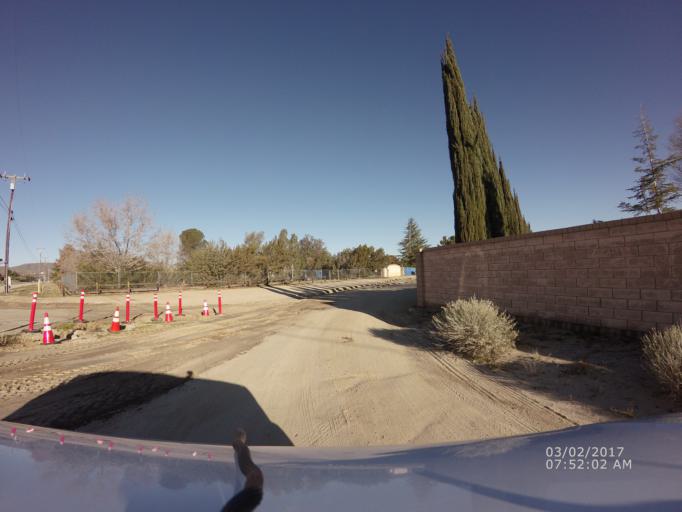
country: US
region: California
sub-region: Los Angeles County
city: Desert View Highlands
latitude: 34.6166
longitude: -118.1744
